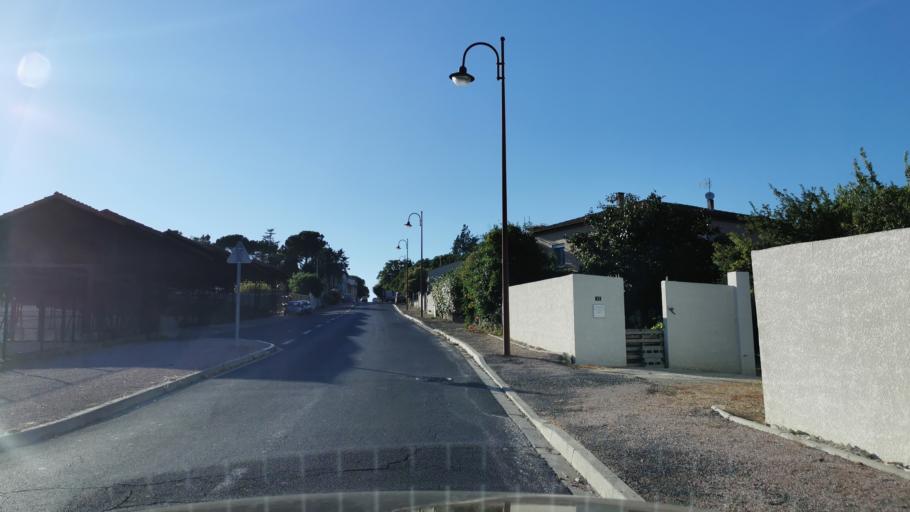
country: FR
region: Languedoc-Roussillon
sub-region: Departement de l'Aude
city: Ouveillan
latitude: 43.2859
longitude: 2.9755
